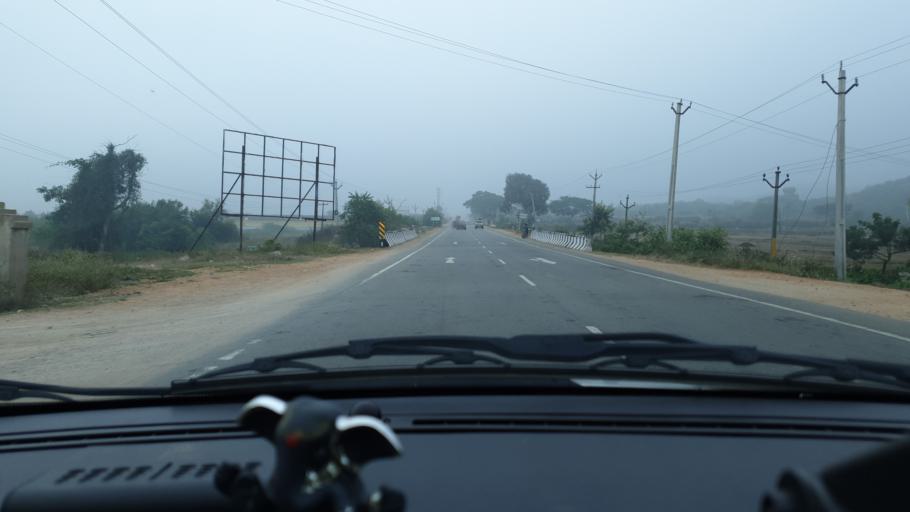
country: IN
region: Telangana
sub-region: Mahbubnagar
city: Farrukhnagar
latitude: 16.9244
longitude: 78.5273
